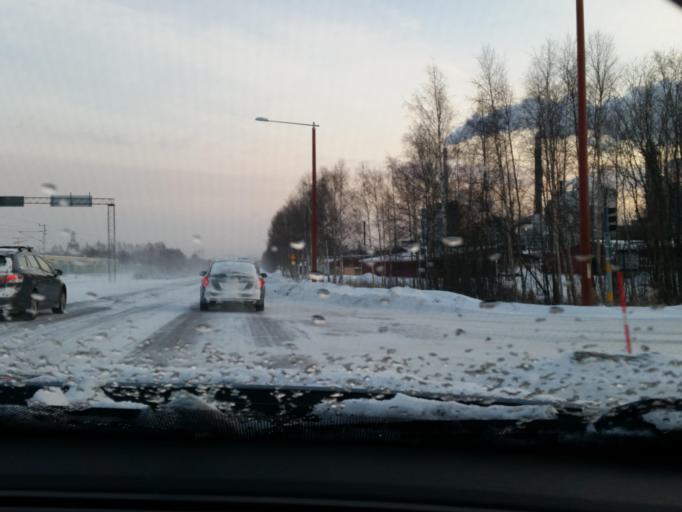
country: SE
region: Norrbotten
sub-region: Pitea Kommun
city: Pitea
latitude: 65.3180
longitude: 21.4436
